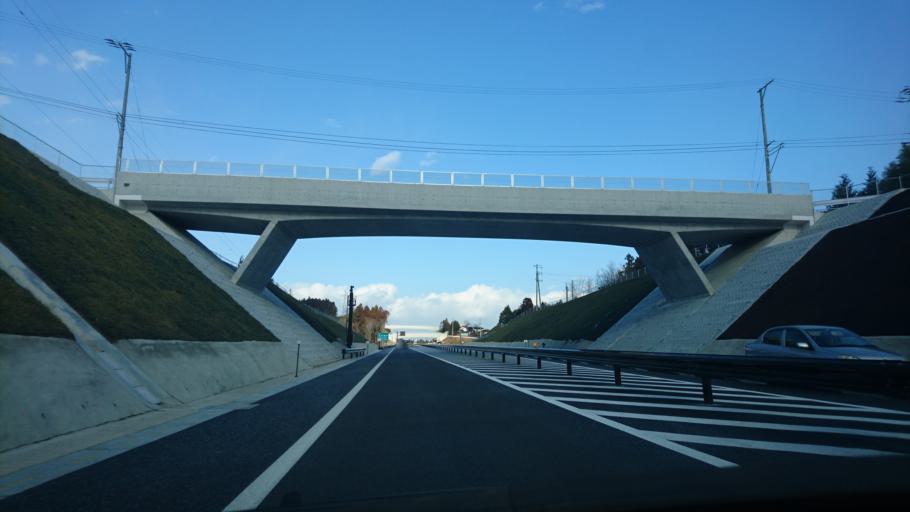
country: JP
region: Iwate
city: Ofunato
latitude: 38.8095
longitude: 141.5467
